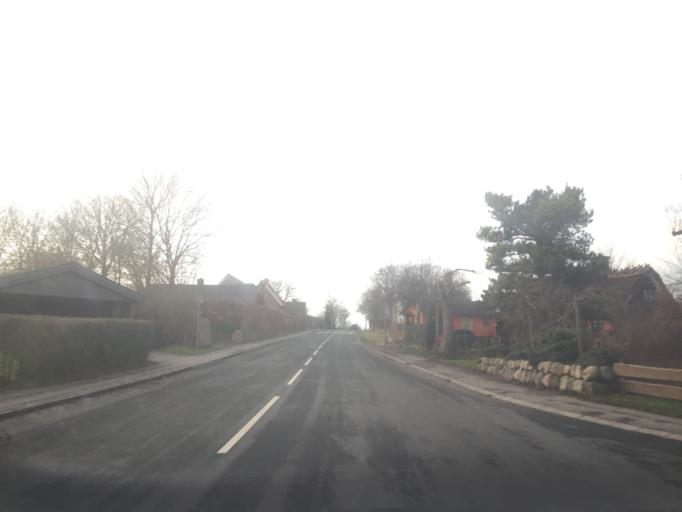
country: DK
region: Capital Region
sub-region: Egedal Kommune
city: Smorumnedre
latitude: 55.7111
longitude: 12.2979
